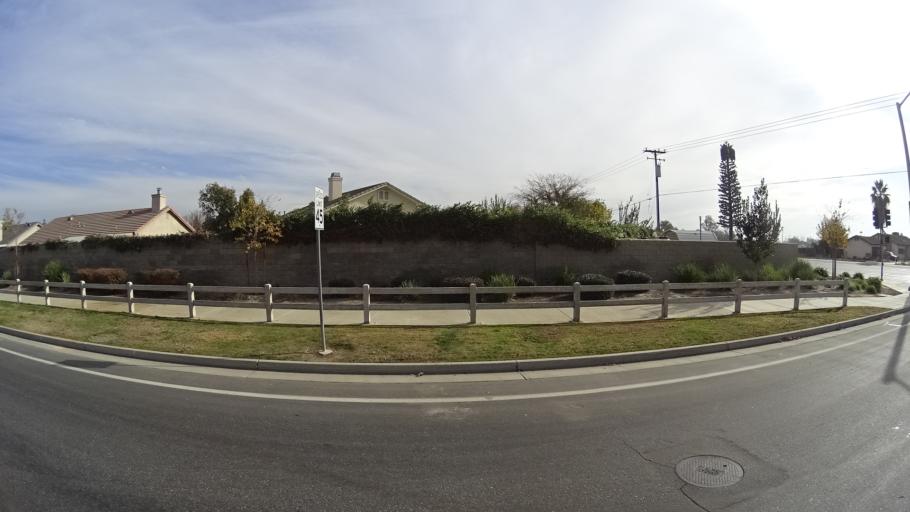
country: US
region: California
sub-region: Kern County
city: Rosedale
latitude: 35.3983
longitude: -119.1278
